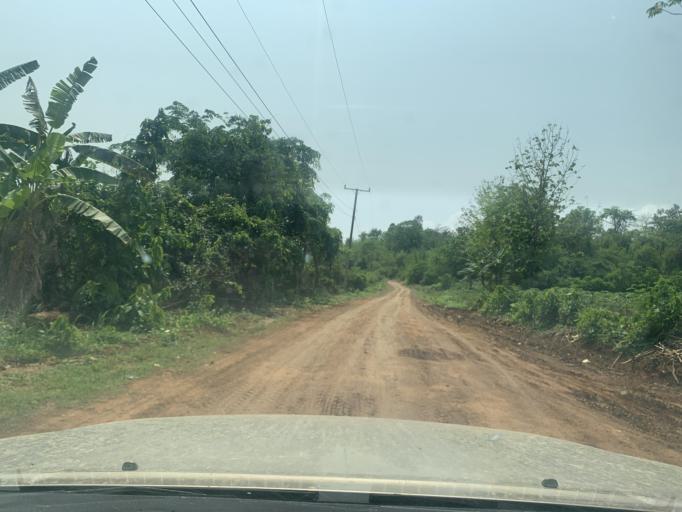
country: TH
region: Uttaradit
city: Ban Khok
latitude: 18.3607
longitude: 101.3875
